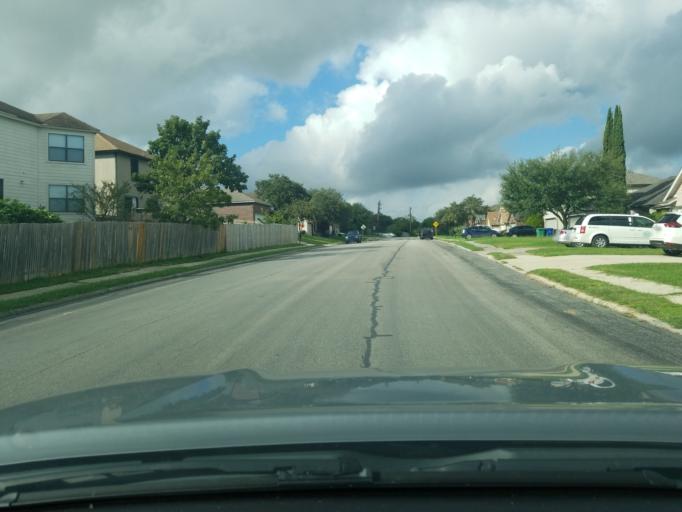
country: US
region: Texas
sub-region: Bexar County
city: Live Oak
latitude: 29.5776
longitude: -98.3593
